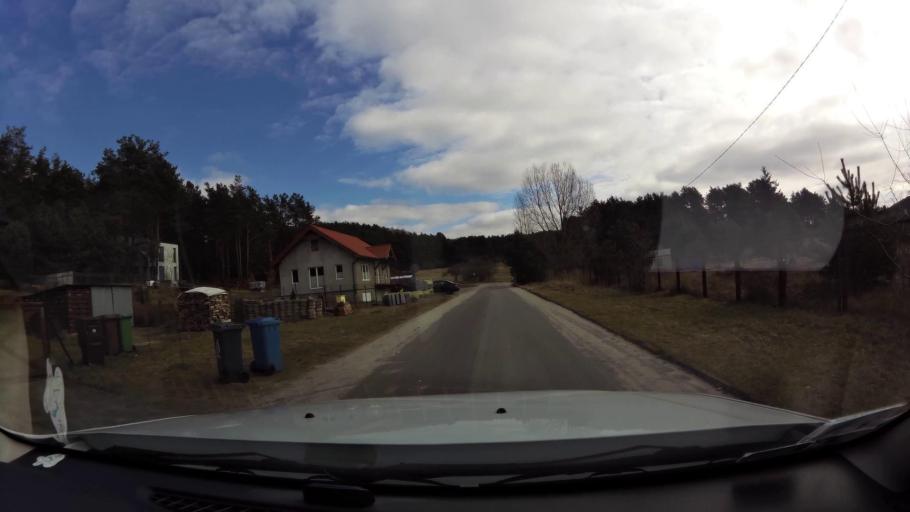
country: PL
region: West Pomeranian Voivodeship
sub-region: Powiat kamienski
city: Miedzyzdroje
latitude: 53.8866
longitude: 14.4455
